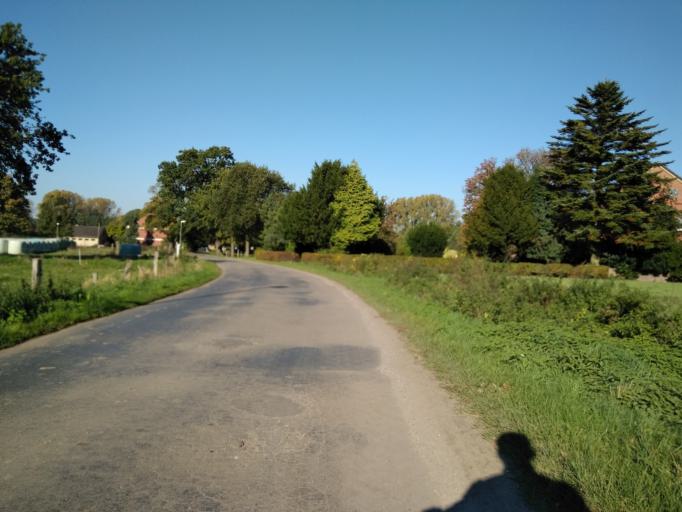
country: DE
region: North Rhine-Westphalia
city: Marl
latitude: 51.6469
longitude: 7.0655
